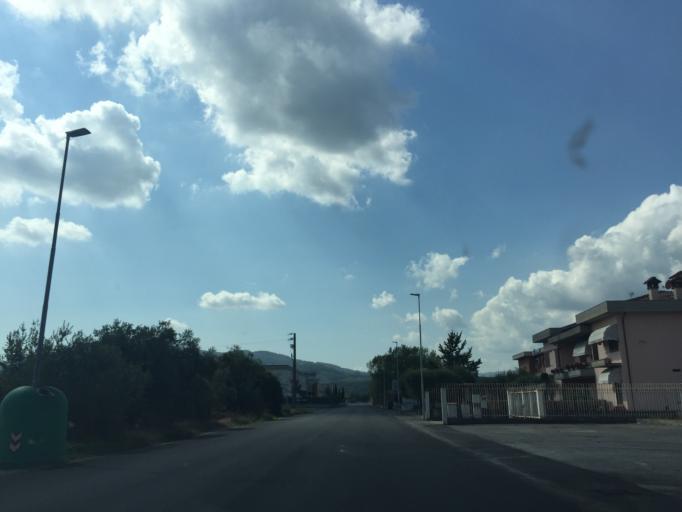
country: IT
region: Tuscany
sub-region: Provincia di Pistoia
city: Cantagrillo-Casalguidi
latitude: 43.8836
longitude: 10.9130
